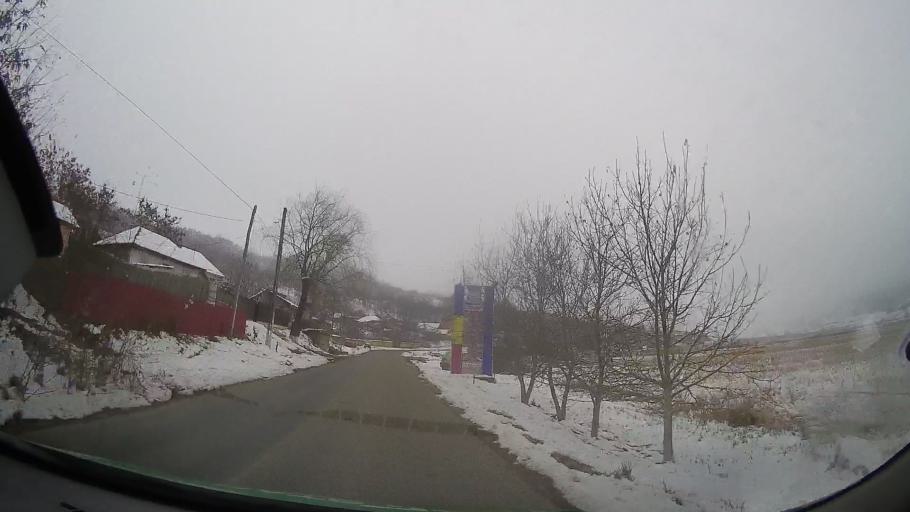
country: RO
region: Bacau
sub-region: Comuna Vultureni
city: Vultureni
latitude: 46.3602
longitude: 27.2880
